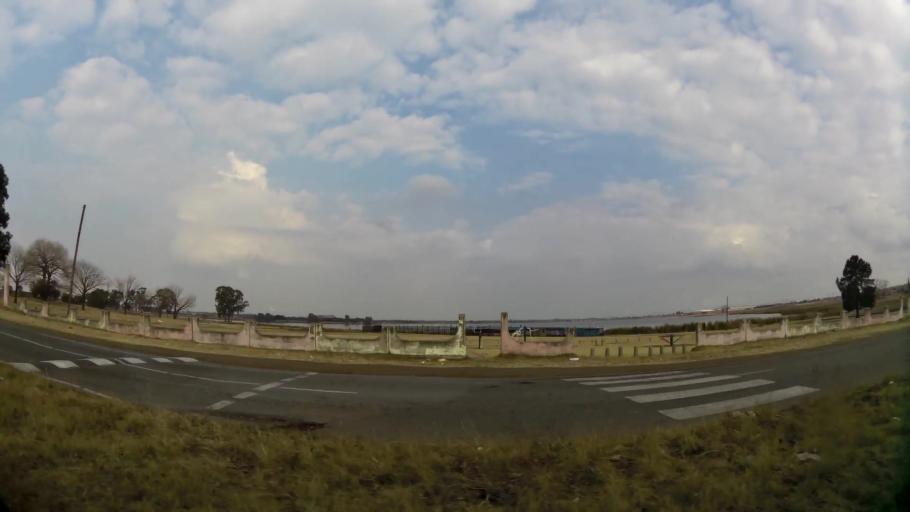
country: ZA
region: Gauteng
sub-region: Sedibeng District Municipality
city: Vereeniging
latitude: -26.6777
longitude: 27.8896
